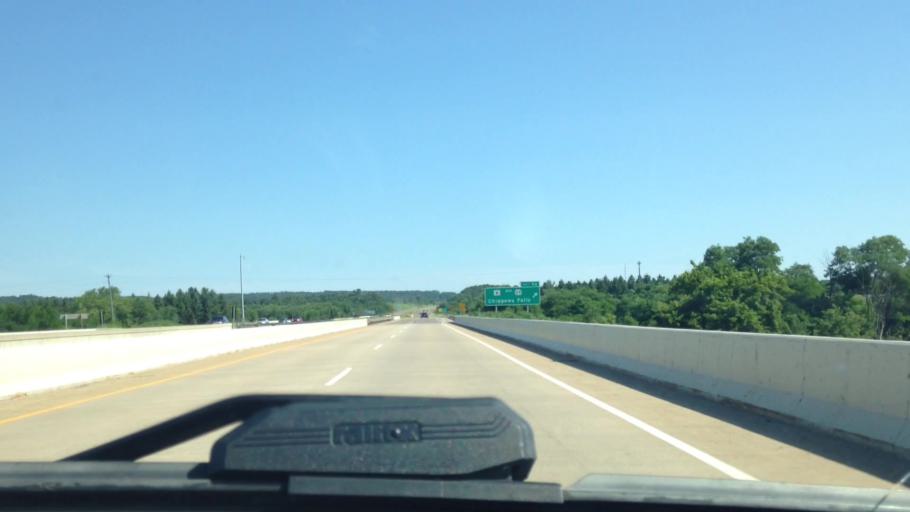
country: US
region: Wisconsin
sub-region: Chippewa County
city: Chippewa Falls
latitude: 44.9216
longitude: -91.4280
